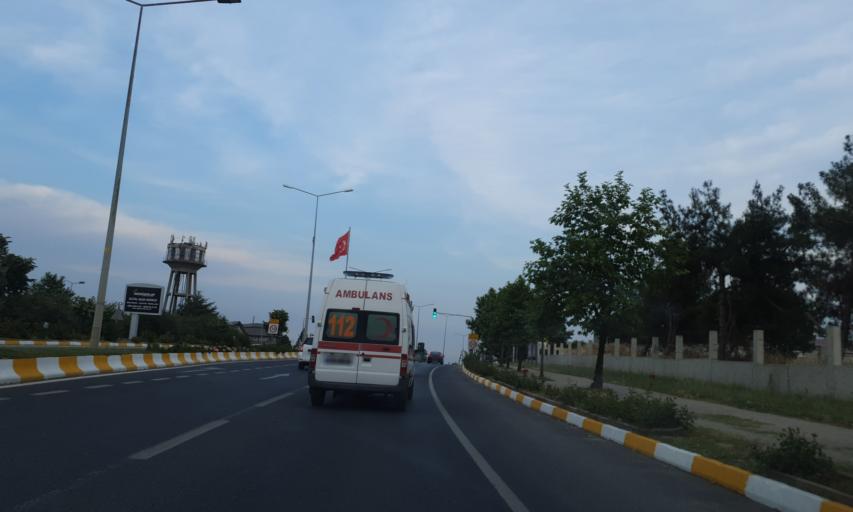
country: TR
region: Kirklareli
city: Luleburgaz
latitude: 41.3995
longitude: 27.3750
